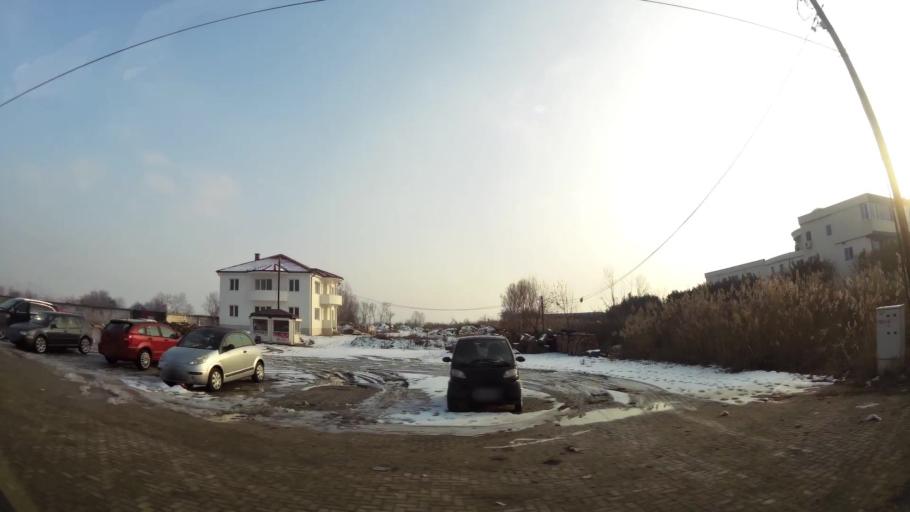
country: MK
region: Aracinovo
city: Arachinovo
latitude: 42.0225
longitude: 21.5484
